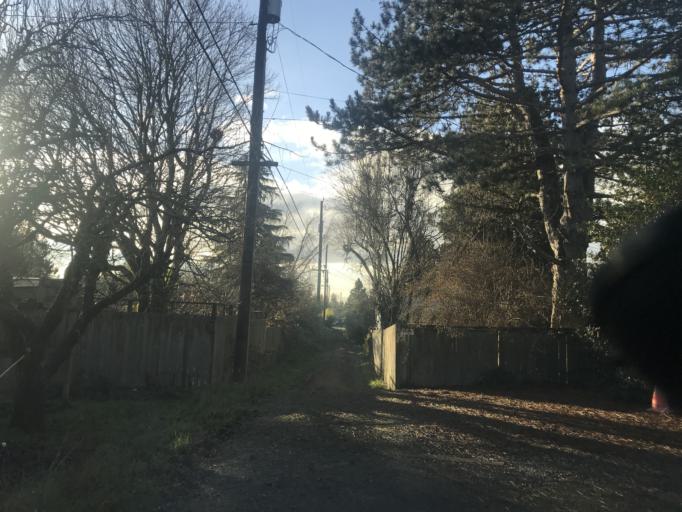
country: US
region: Washington
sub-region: King County
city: White Center
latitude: 47.5223
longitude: -122.3726
